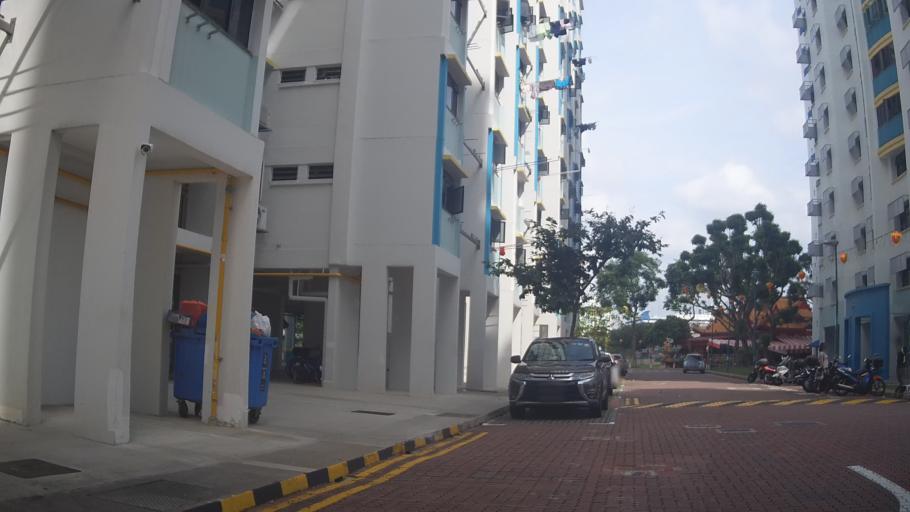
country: SG
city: Singapore
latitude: 1.3141
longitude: 103.8701
